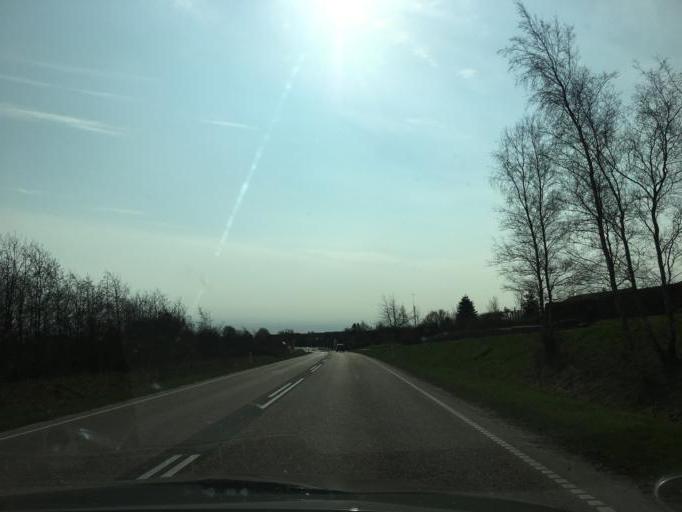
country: DK
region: South Denmark
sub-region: Vejen Kommune
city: Vejen
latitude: 55.4879
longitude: 9.1341
